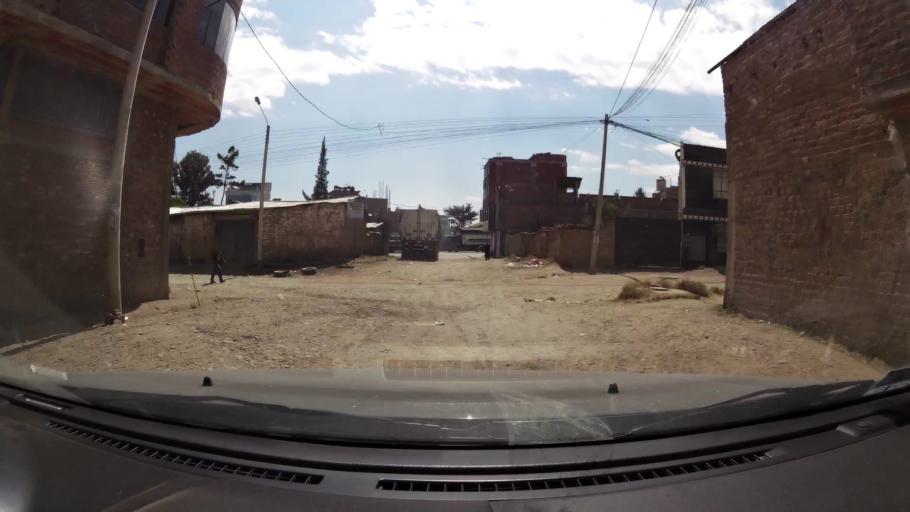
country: PE
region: Junin
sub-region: Provincia de Huancayo
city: Huancayo
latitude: -12.0655
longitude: -75.2003
